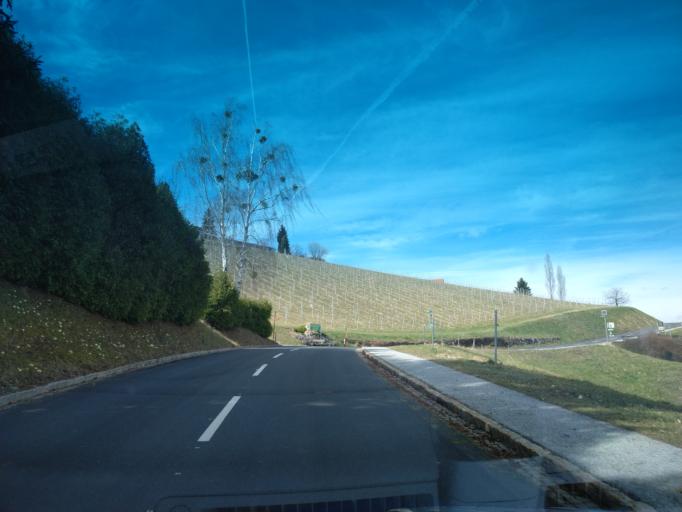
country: AT
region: Styria
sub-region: Politischer Bezirk Leibnitz
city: Kitzeck im Sausal
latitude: 46.7889
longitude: 15.4449
